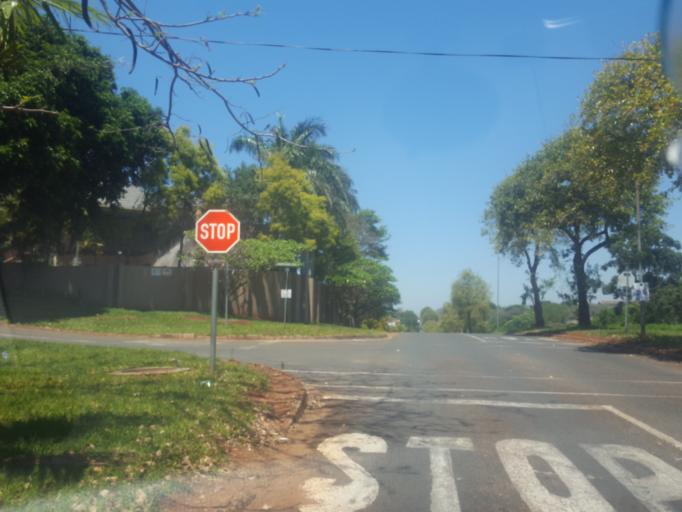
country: ZA
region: KwaZulu-Natal
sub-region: uThungulu District Municipality
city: Empangeni
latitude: -28.7496
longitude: 31.9023
